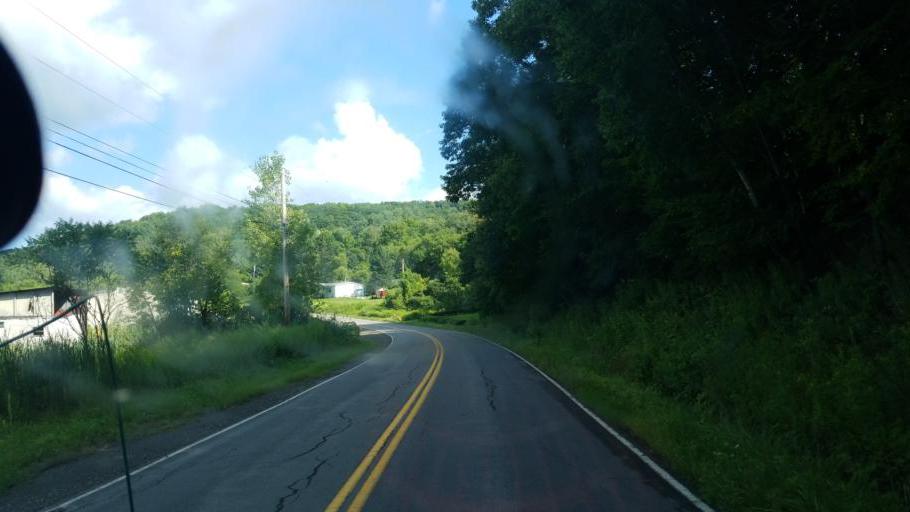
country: US
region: New York
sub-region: Steuben County
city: Canisteo
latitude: 42.2832
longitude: -77.6046
